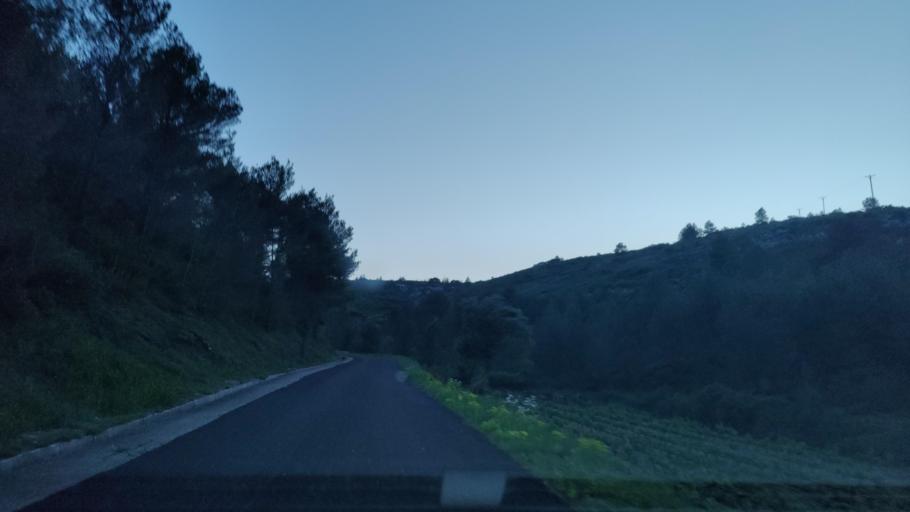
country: FR
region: Languedoc-Roussillon
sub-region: Departement des Pyrenees-Orientales
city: Estagel
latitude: 42.8537
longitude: 2.7703
